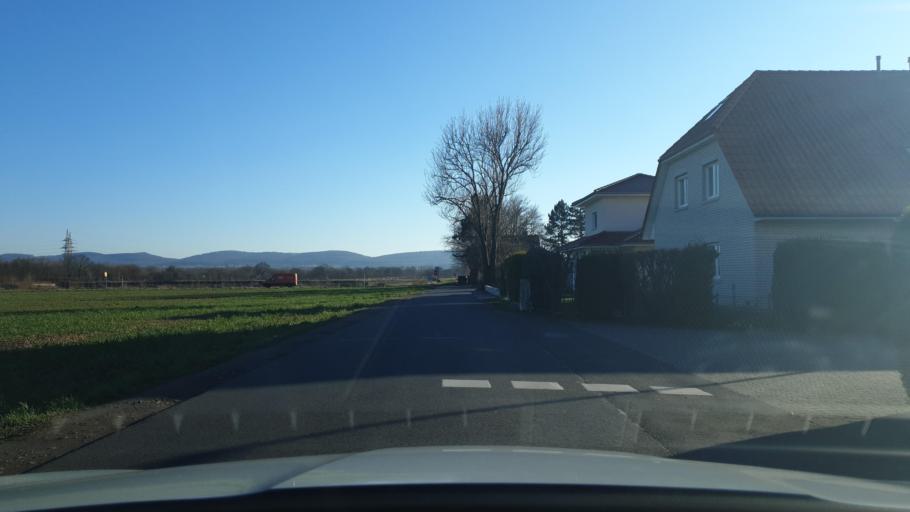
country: DE
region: North Rhine-Westphalia
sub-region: Regierungsbezirk Detmold
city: Minden
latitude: 52.2890
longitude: 8.9685
